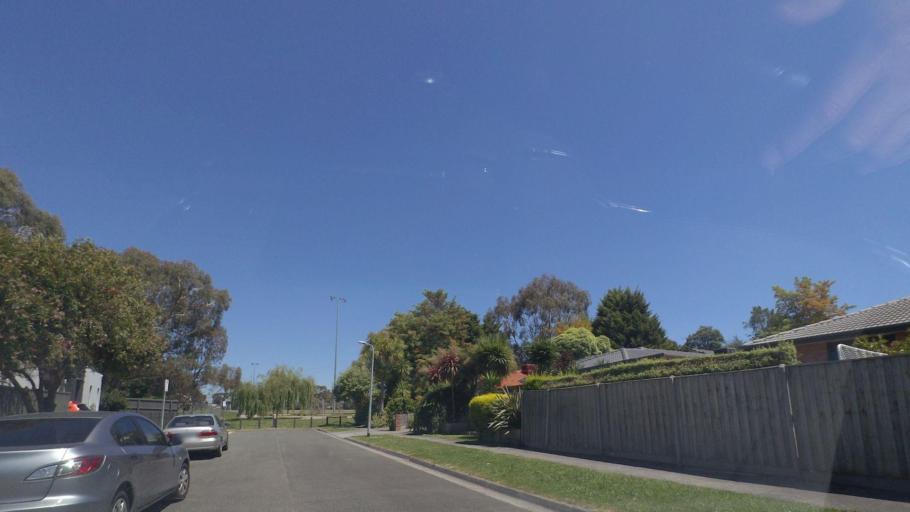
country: AU
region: Victoria
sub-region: Knox
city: Knoxfield
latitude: -37.8961
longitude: 145.2600
